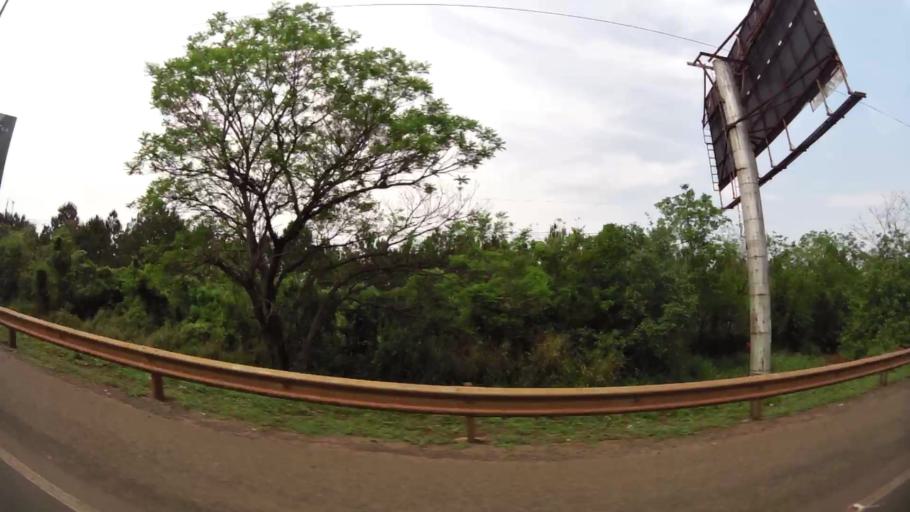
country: PY
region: Alto Parana
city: Ciudad del Este
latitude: -25.4850
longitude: -54.6277
